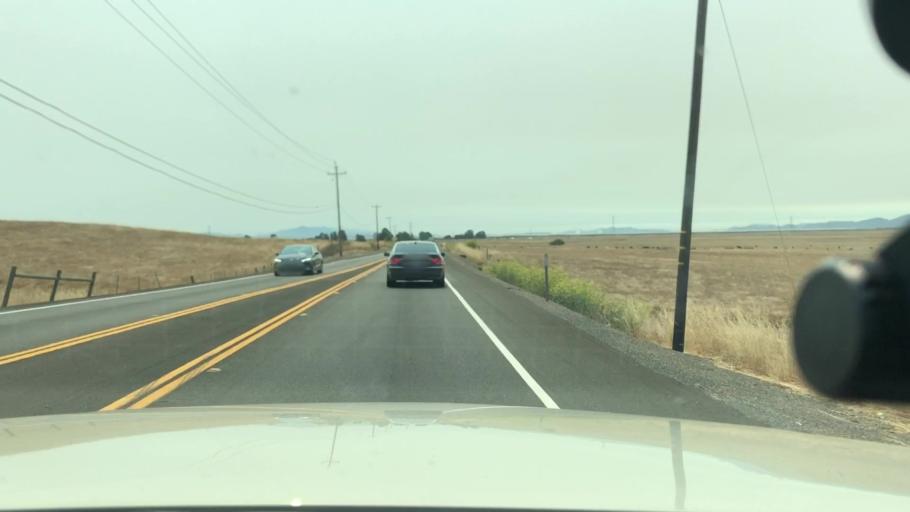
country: US
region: California
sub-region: Marin County
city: Black Point-Green Point
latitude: 38.1508
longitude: -122.4889
